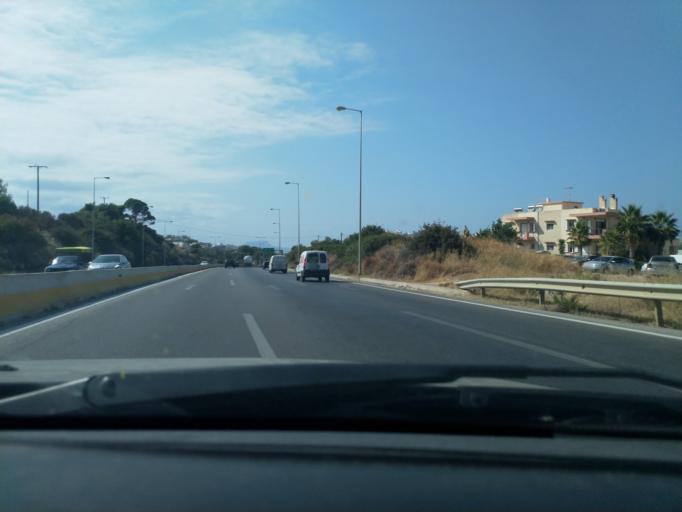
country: GR
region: Crete
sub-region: Nomos Rethymnis
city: Atsipopoulon
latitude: 35.3601
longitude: 24.4492
